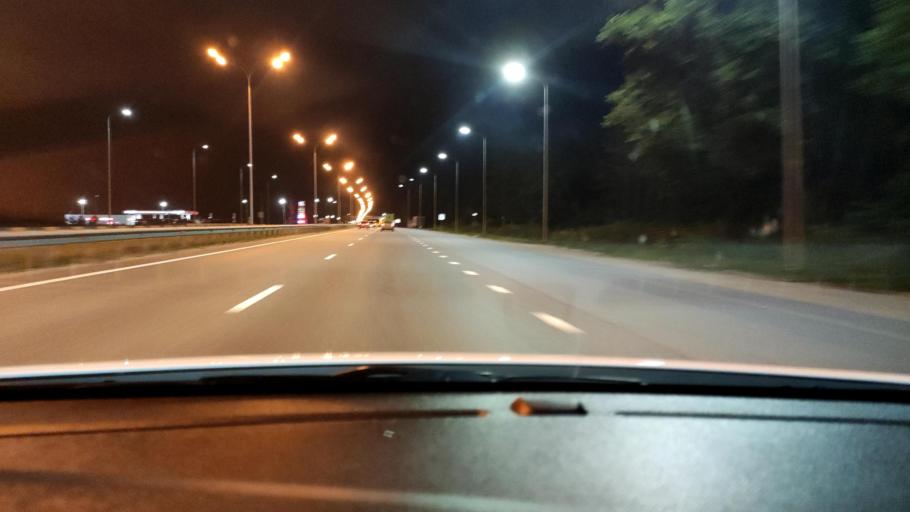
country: RU
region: Tatarstan
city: Sviyazhsk
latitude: 55.7540
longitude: 48.8052
